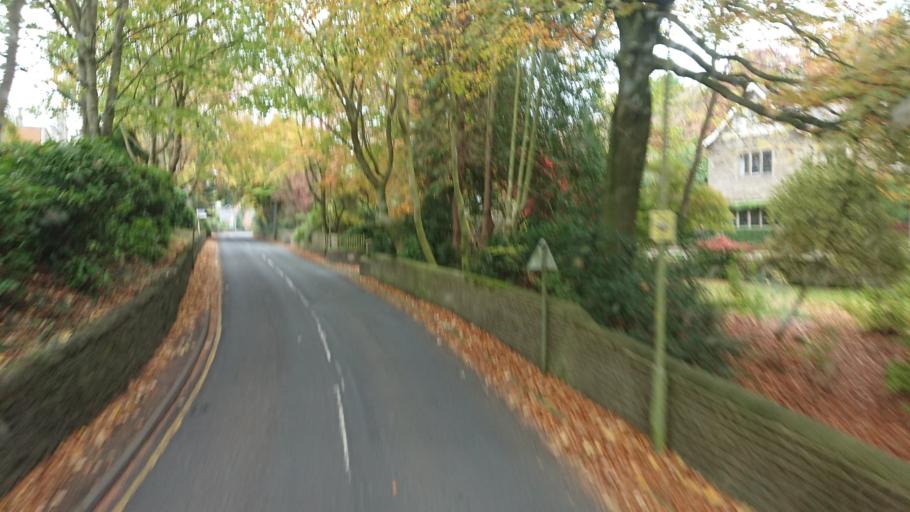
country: GB
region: England
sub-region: North Yorkshire
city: Skipton
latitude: 53.9652
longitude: -2.0213
